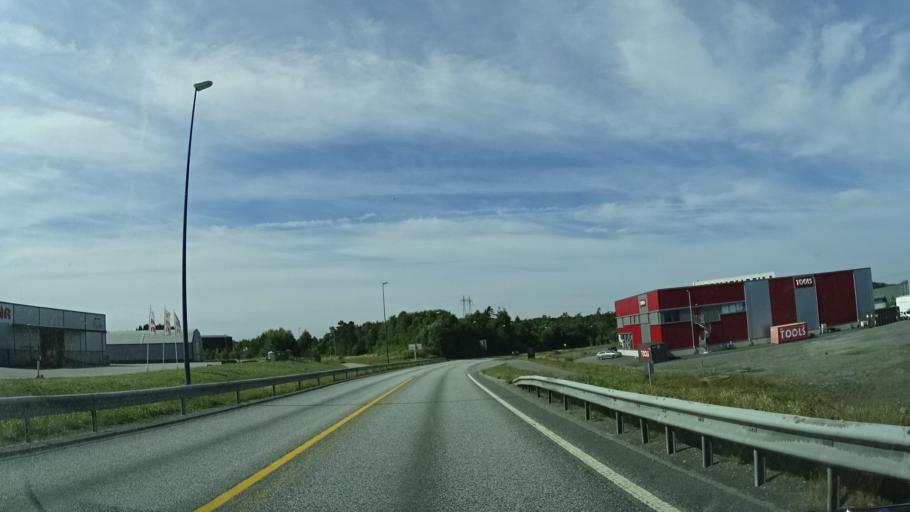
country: NO
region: Hordaland
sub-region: Stord
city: Leirvik
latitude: 59.7611
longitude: 5.4494
